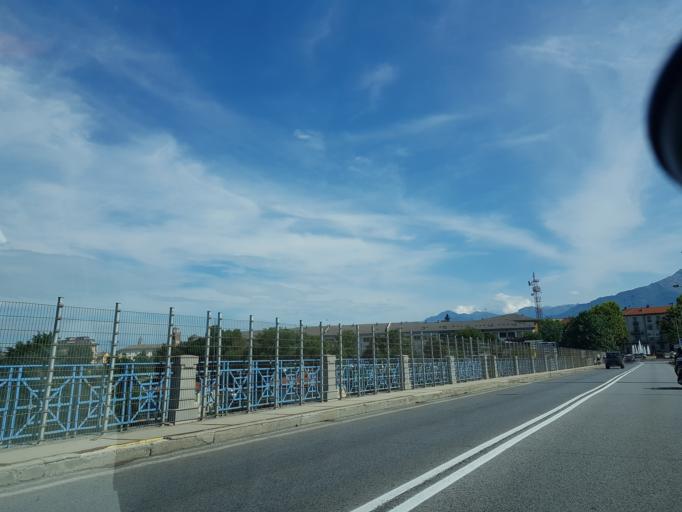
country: IT
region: Piedmont
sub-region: Provincia di Cuneo
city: Cuneo
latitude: 44.3928
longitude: 7.5418
